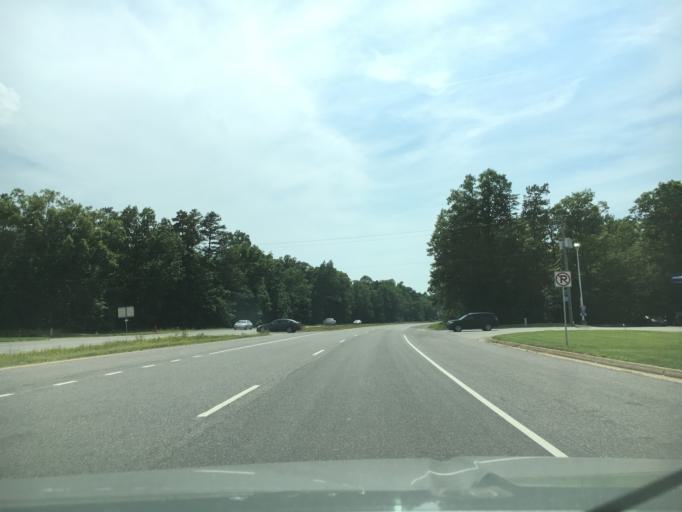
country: US
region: Virginia
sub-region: Amelia County
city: Amelia Court House
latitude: 37.3581
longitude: -77.9601
